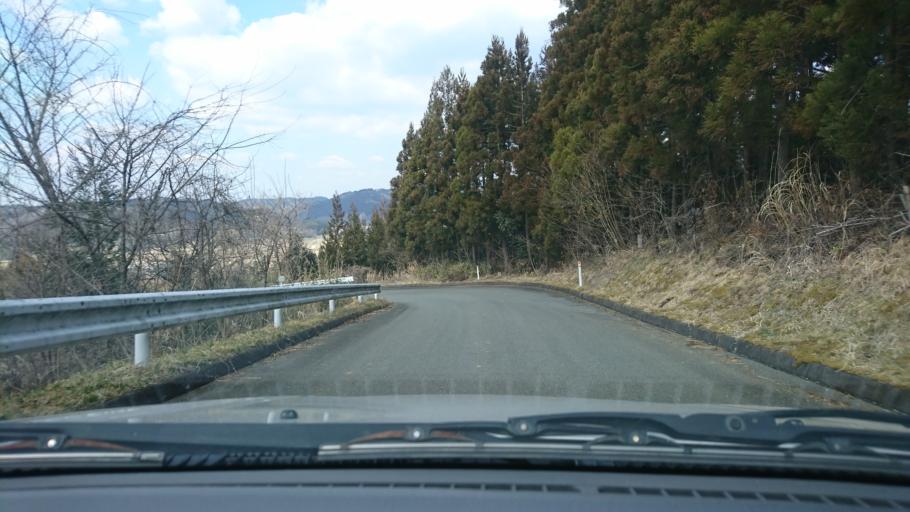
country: JP
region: Iwate
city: Ichinoseki
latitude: 38.8260
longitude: 141.2587
